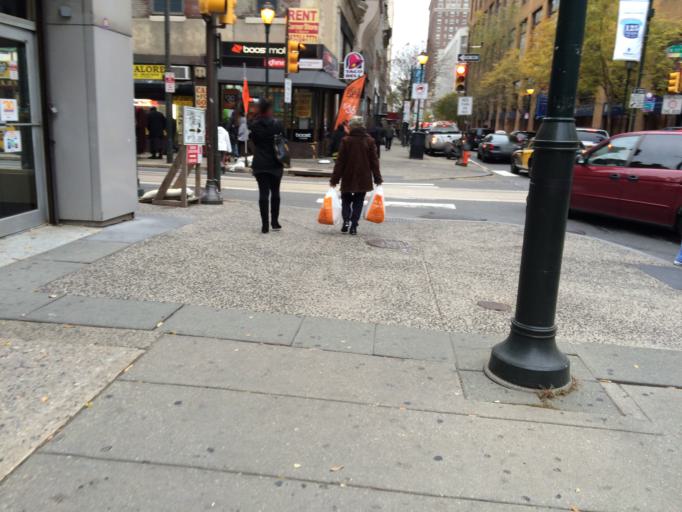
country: US
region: Pennsylvania
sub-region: Philadelphia County
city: Philadelphia
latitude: 39.9502
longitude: -75.1589
